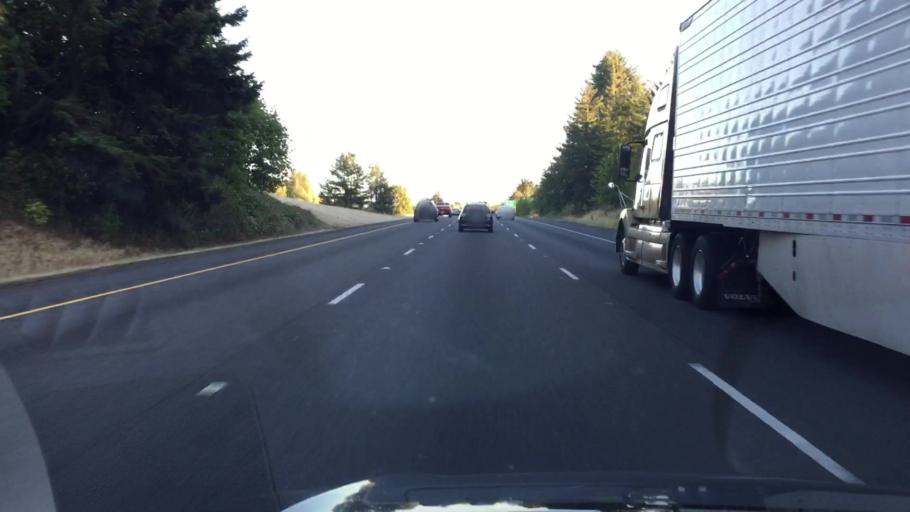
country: US
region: Washington
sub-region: Clark County
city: La Center
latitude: 45.8619
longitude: -122.7063
